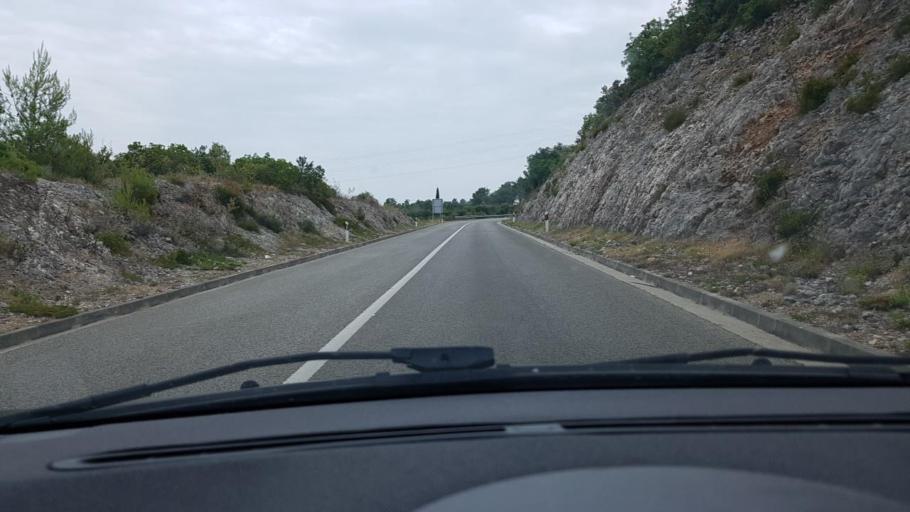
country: HR
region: Dubrovacko-Neretvanska
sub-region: Grad Korcula
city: Zrnovo
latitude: 42.9474
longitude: 17.1199
